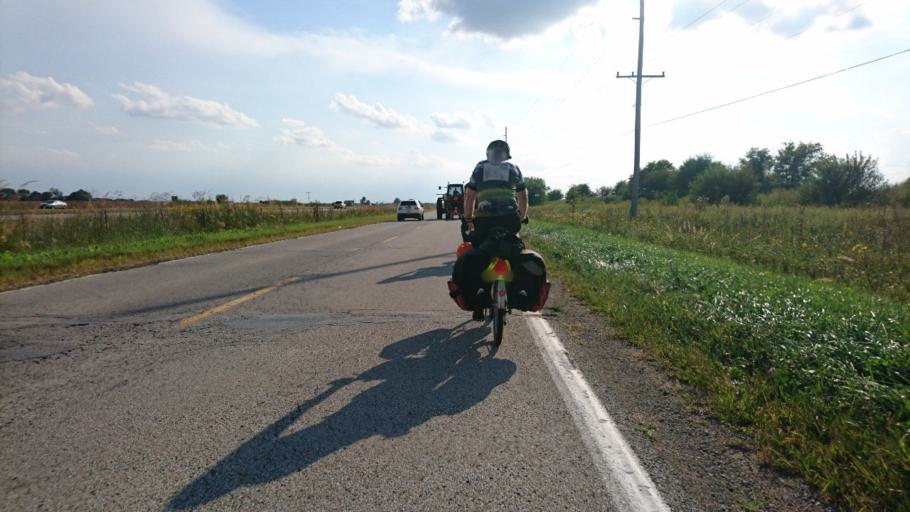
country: US
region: Illinois
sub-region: Logan County
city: Atlanta
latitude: 40.3009
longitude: -89.1852
